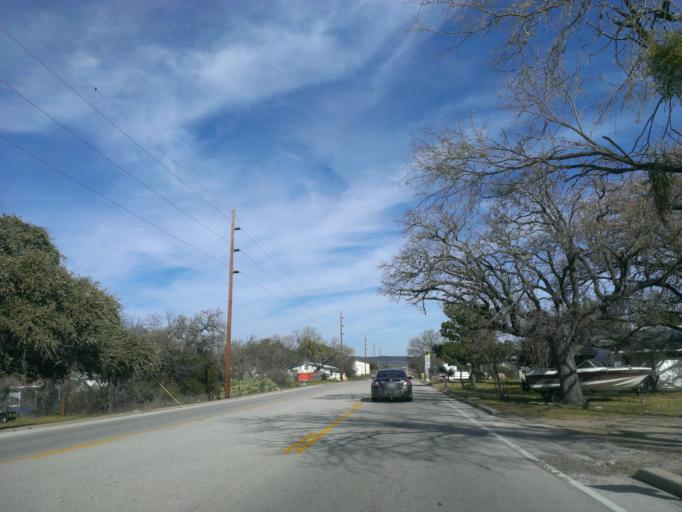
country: US
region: Texas
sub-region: Llano County
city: Kingsland
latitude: 30.6499
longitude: -98.4470
